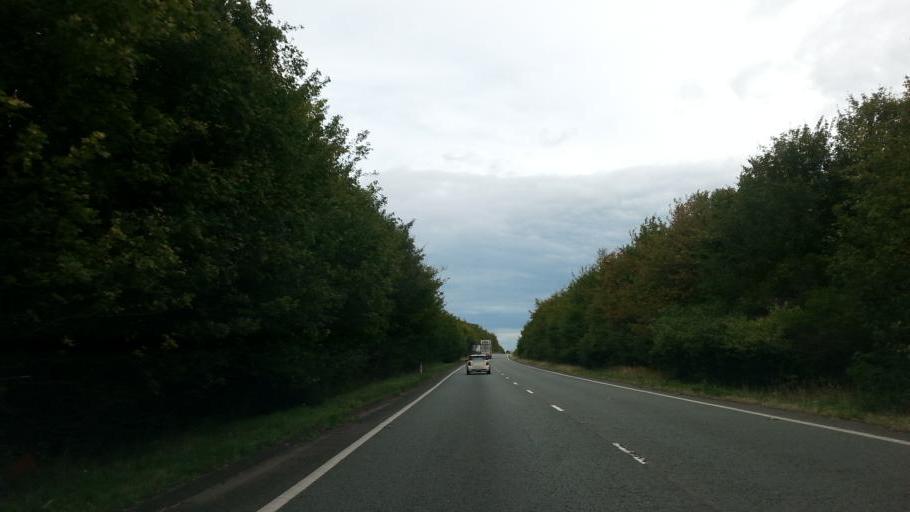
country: GB
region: England
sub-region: Cambridgeshire
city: Duxford
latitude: 52.0913
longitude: 0.2024
